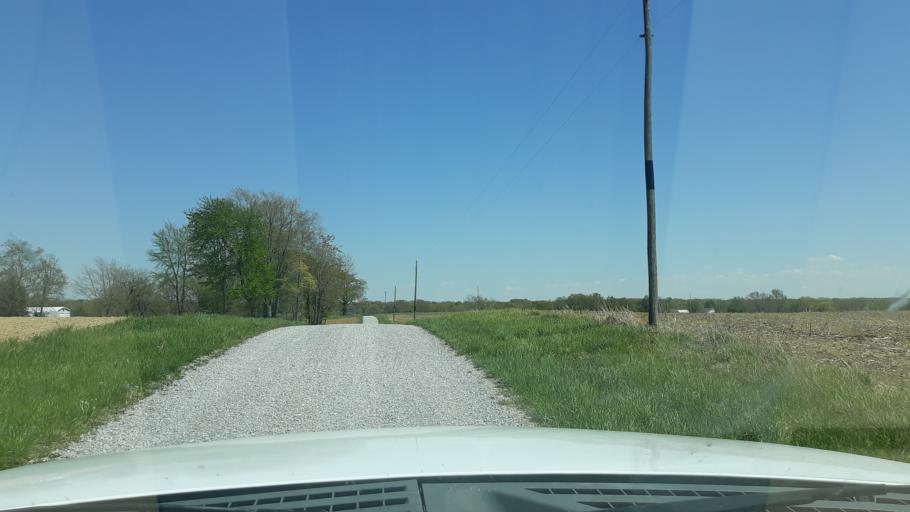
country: US
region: Illinois
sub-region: Saline County
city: Harrisburg
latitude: 37.8849
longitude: -88.6455
